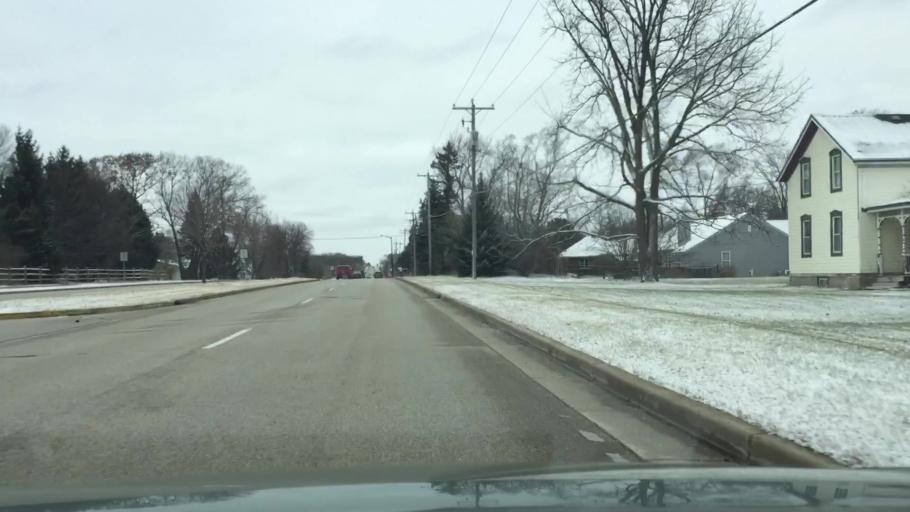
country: US
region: Wisconsin
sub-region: Waukesha County
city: Butler
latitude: 43.1145
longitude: -88.1053
